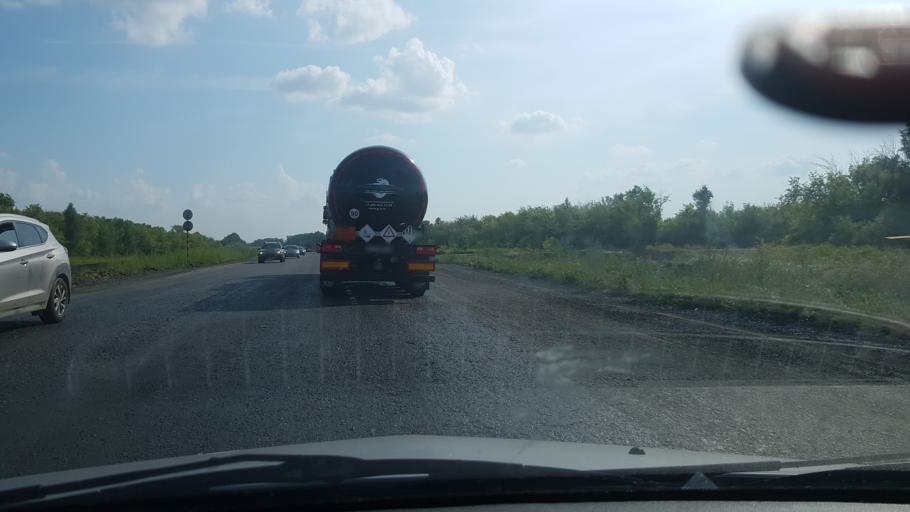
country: RU
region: Chuvashia
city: Shikhazany
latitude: 55.6947
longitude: 47.4336
